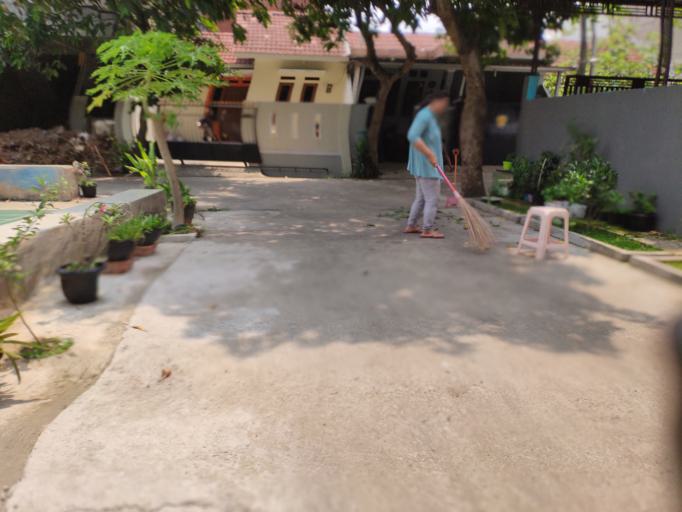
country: ID
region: West Java
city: Sawangan
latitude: -6.3707
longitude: 106.7930
